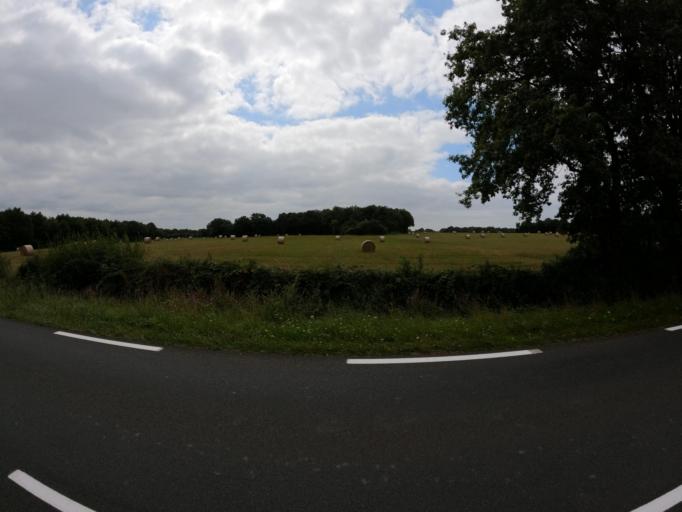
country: FR
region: Poitou-Charentes
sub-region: Departement de la Vienne
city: Charroux
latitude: 46.1262
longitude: 0.4944
